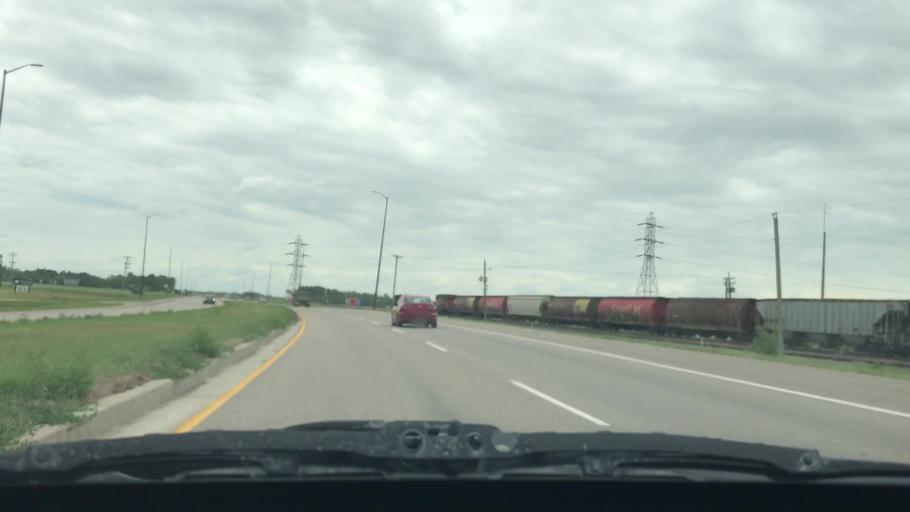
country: CA
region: Manitoba
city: Winnipeg
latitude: 49.8427
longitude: -96.9902
